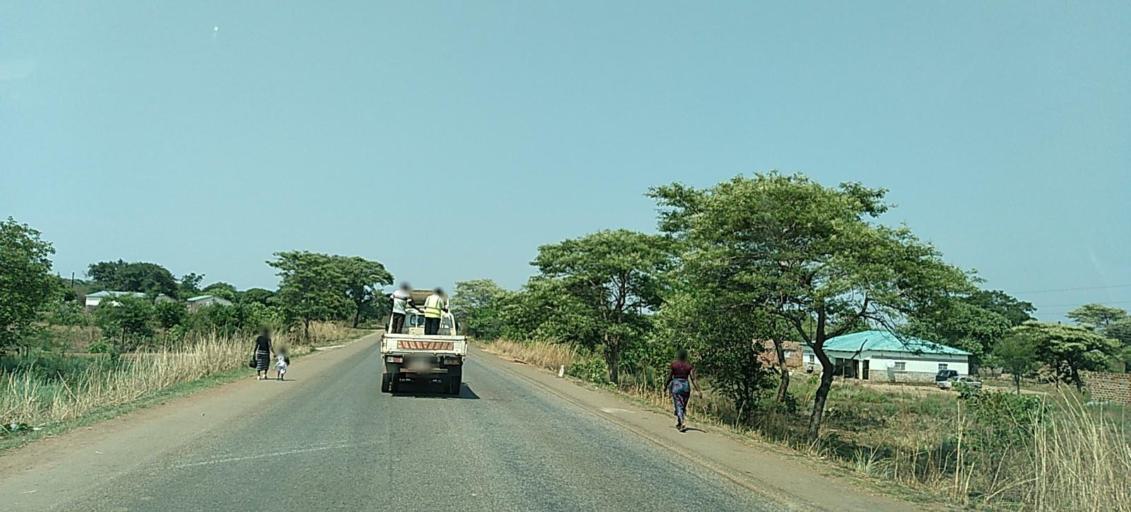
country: ZM
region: Copperbelt
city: Mpongwe
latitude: -13.4377
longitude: 28.2371
